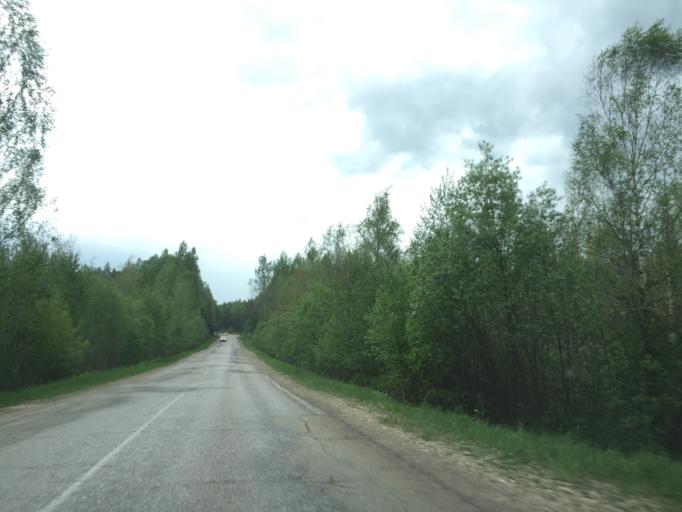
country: LV
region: Ogre
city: Ogre
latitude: 56.8404
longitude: 24.5761
